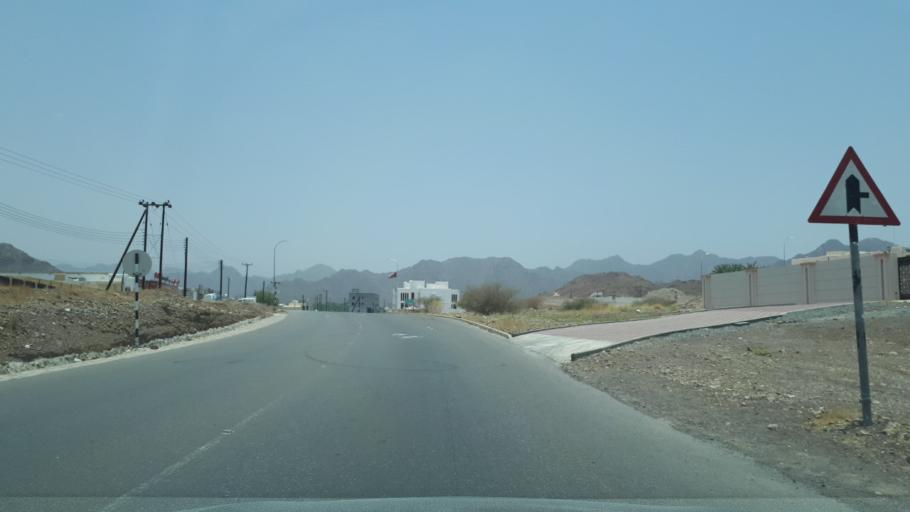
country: OM
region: Al Batinah
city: Rustaq
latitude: 23.4245
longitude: 57.2896
